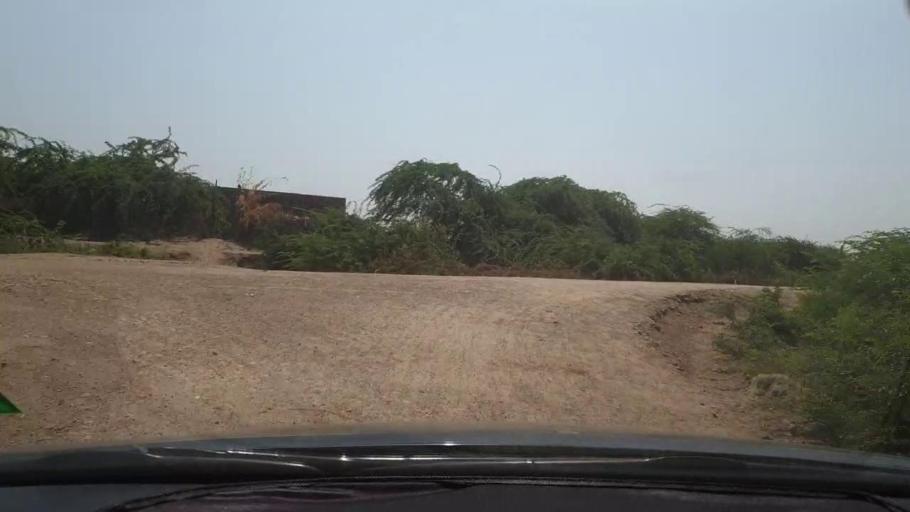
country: PK
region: Sindh
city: Tando Bago
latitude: 24.8013
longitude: 69.1840
